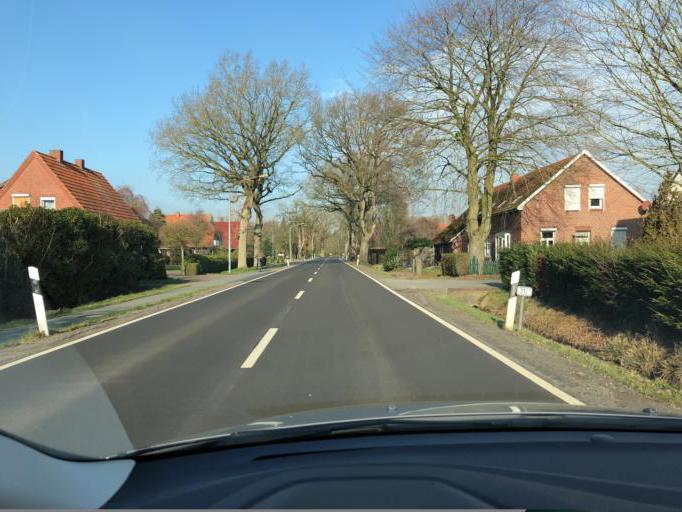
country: DE
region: Lower Saxony
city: Westerstede
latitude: 53.2747
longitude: 7.9034
